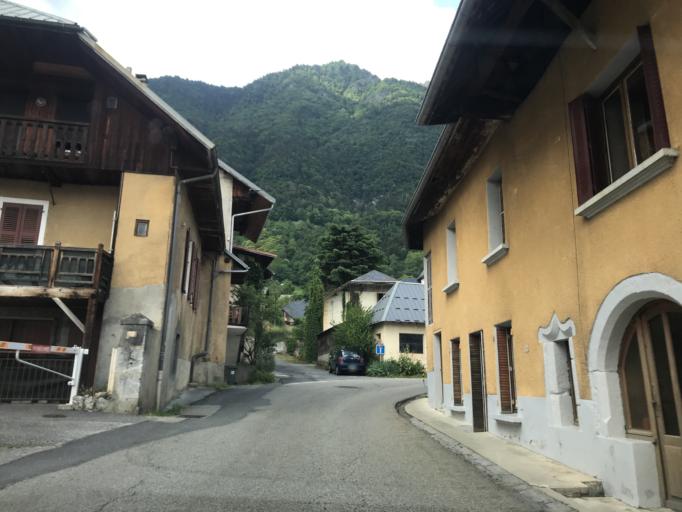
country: FR
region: Rhone-Alpes
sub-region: Departement de la Savoie
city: Mercury
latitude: 45.6755
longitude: 6.3364
